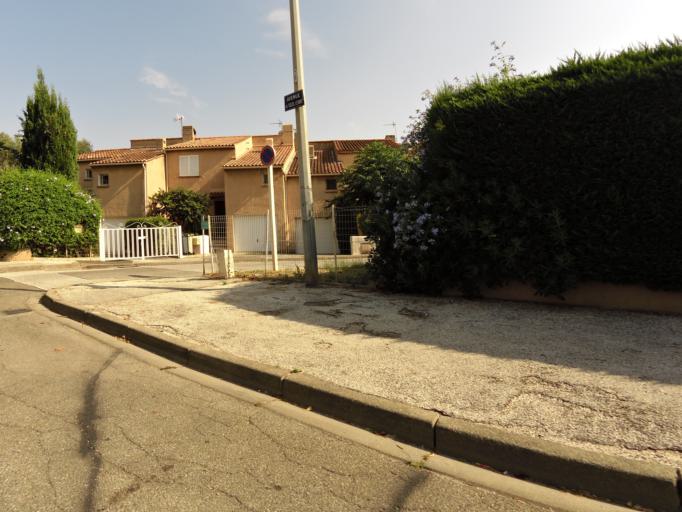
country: FR
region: Provence-Alpes-Cote d'Azur
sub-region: Departement du Var
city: Hyeres
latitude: 43.1174
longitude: 6.1419
